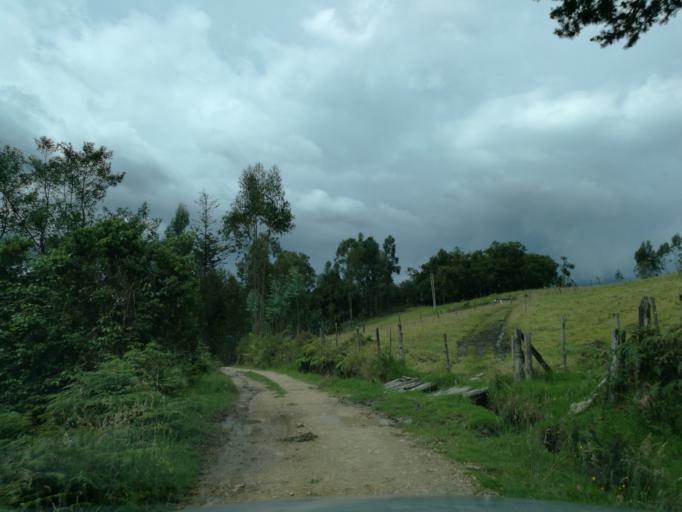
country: CO
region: Boyaca
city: Arcabuco
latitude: 5.7487
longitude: -73.4621
